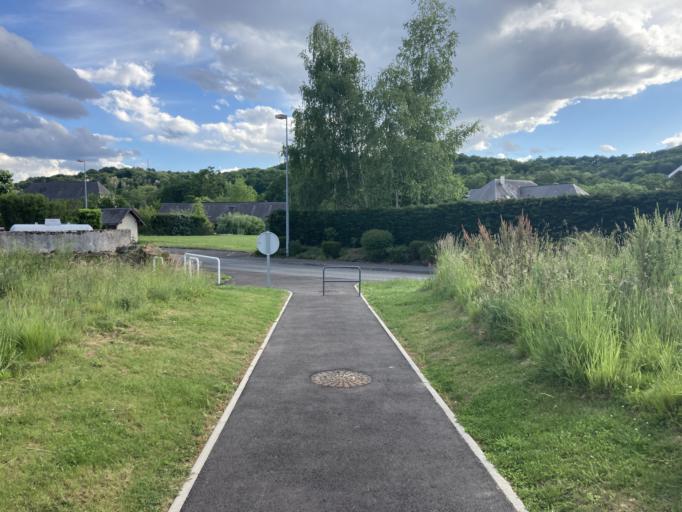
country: FR
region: Aquitaine
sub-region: Departement des Pyrenees-Atlantiques
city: Artiguelouve
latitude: 43.3215
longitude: -0.4804
